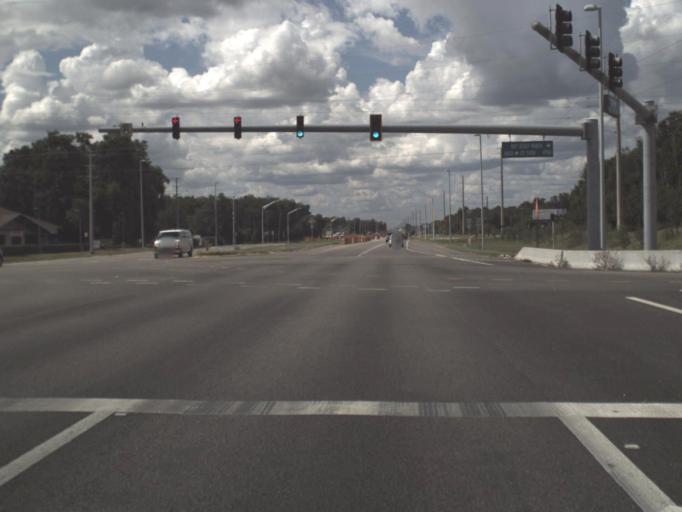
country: US
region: Florida
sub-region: Polk County
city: Highland City
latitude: 27.9527
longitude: -81.8697
